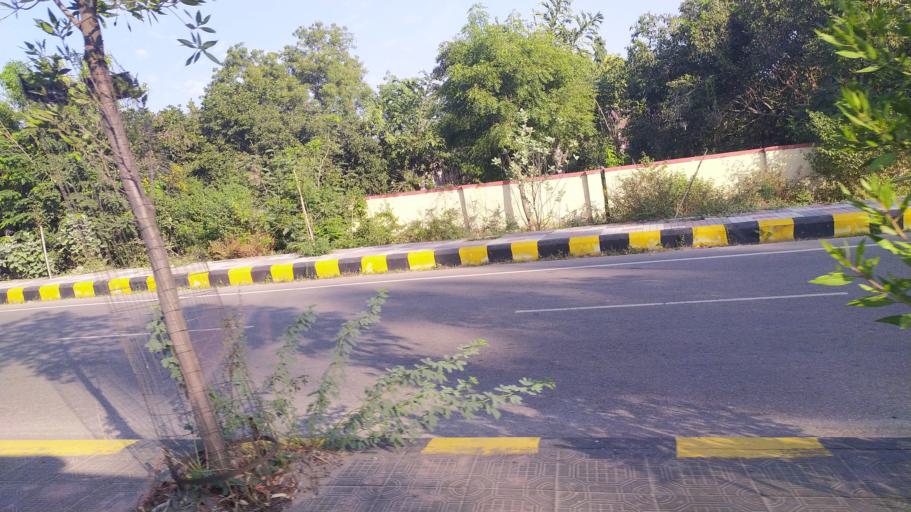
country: IN
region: Telangana
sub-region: Hyderabad
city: Hyderabad
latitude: 17.3196
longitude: 78.3934
